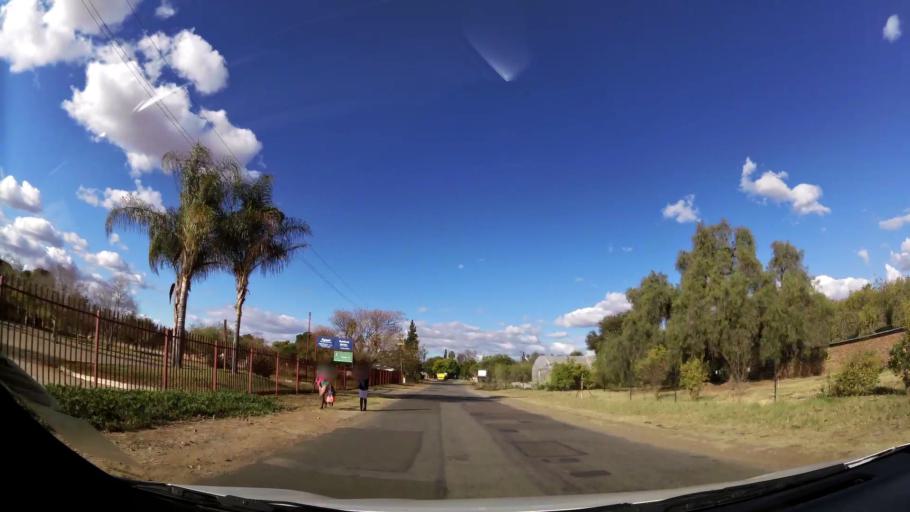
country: ZA
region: Limpopo
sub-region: Capricorn District Municipality
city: Polokwane
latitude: -23.9299
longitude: 29.4487
